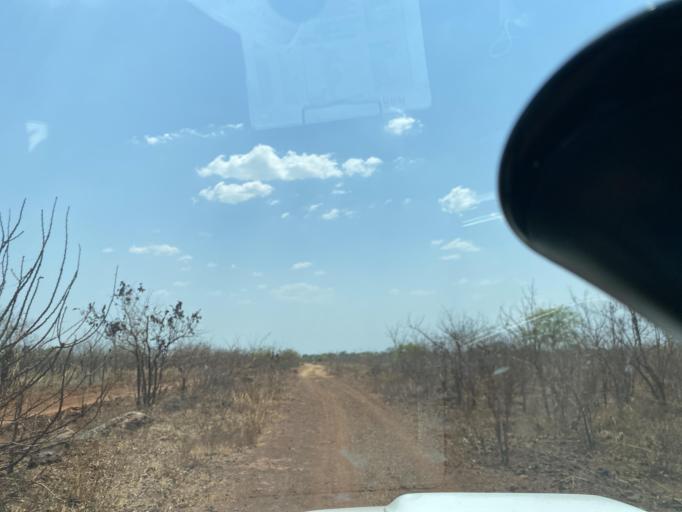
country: ZM
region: Lusaka
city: Lusaka
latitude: -15.4980
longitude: 27.9602
